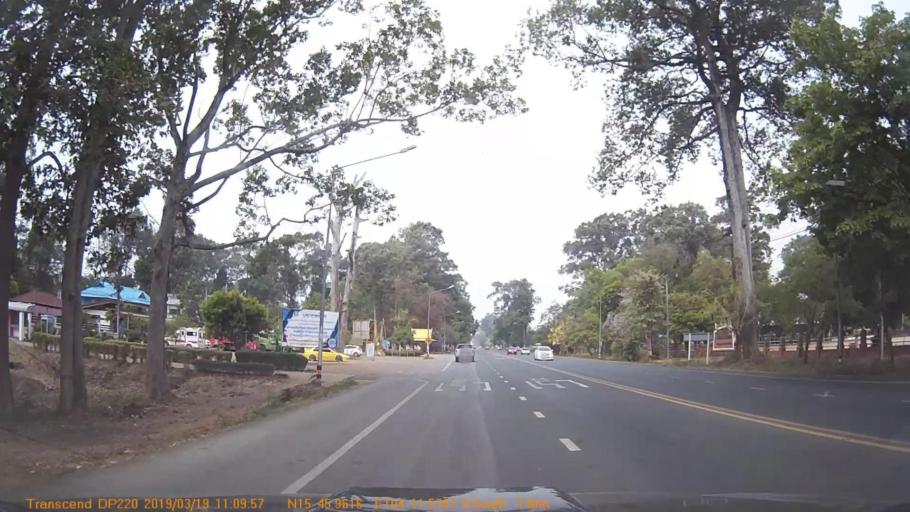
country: TH
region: Yasothon
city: Yasothon
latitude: 15.7661
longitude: 104.1927
